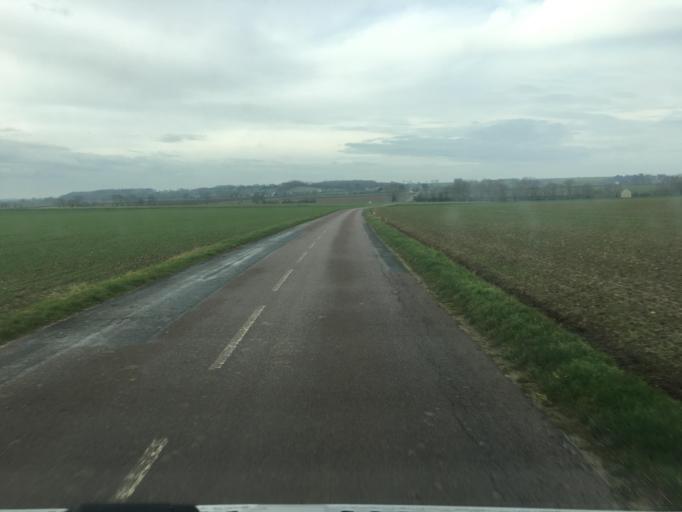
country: FR
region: Lower Normandy
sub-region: Departement du Calvados
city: Ver-sur-Mer
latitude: 49.3284
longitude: -0.5801
